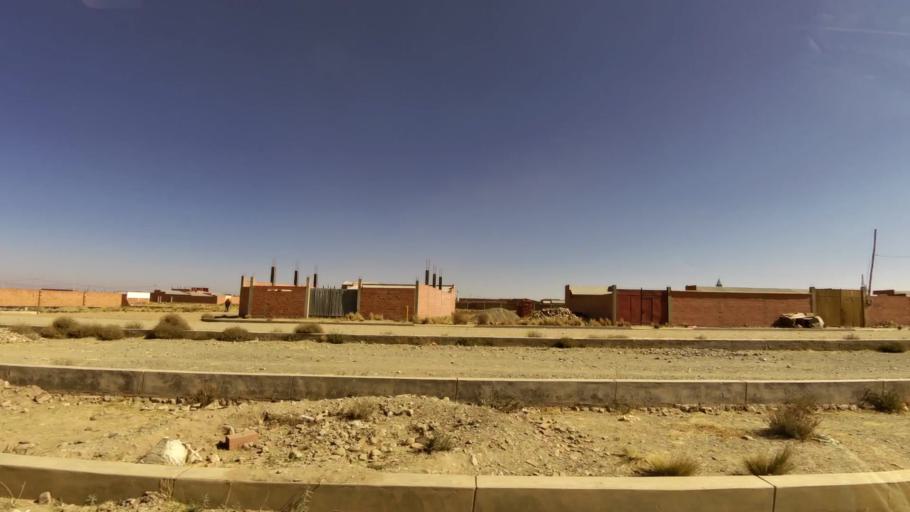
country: BO
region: La Paz
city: La Paz
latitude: -16.5987
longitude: -68.2002
